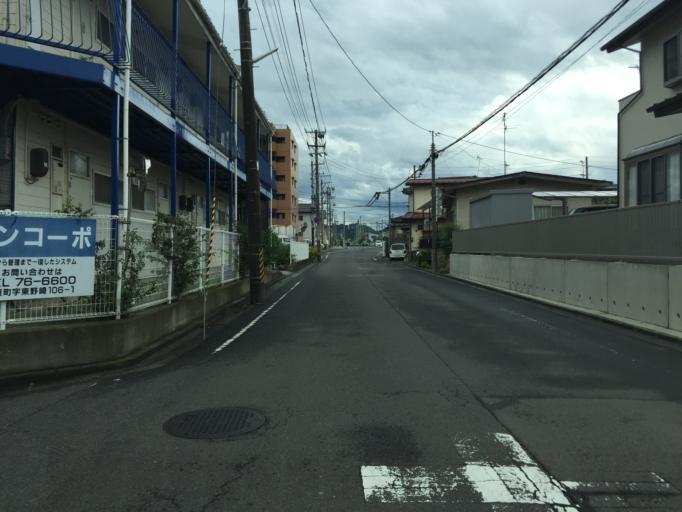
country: JP
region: Fukushima
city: Fukushima-shi
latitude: 37.7615
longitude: 140.4850
